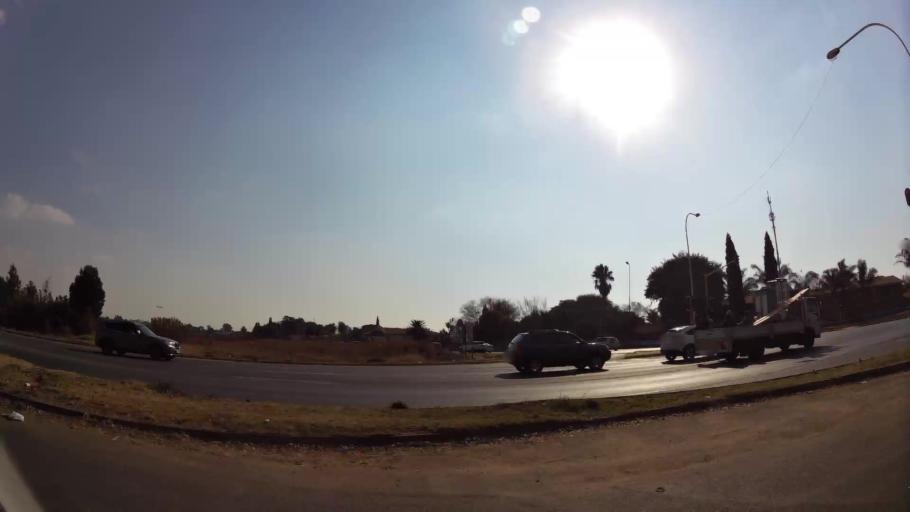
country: ZA
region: Gauteng
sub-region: Ekurhuleni Metropolitan Municipality
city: Boksburg
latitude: -26.1795
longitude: 28.2672
